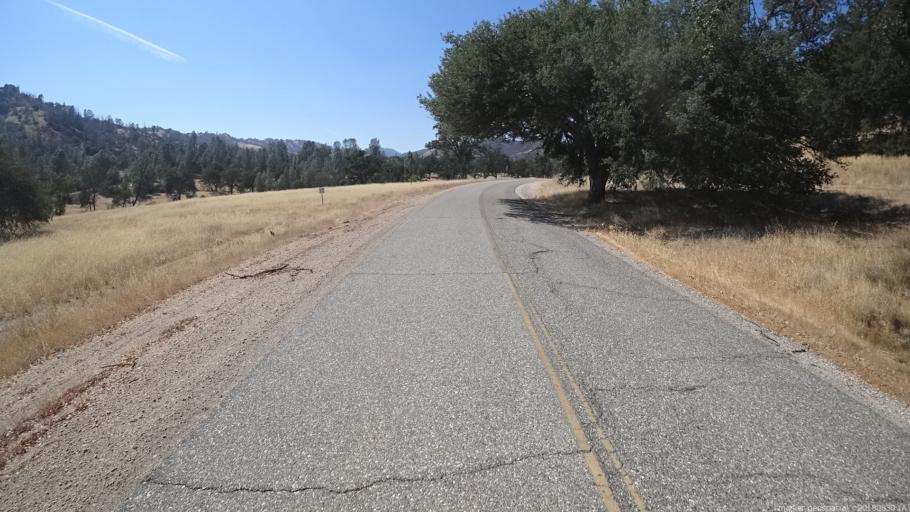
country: US
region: California
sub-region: Monterey County
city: King City
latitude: 36.0064
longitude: -121.2749
